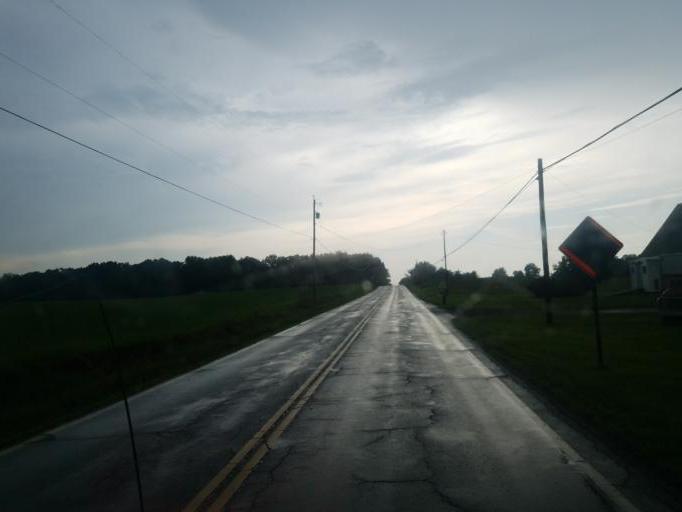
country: US
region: Ohio
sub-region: Wayne County
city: Creston
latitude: 40.9453
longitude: -81.9041
